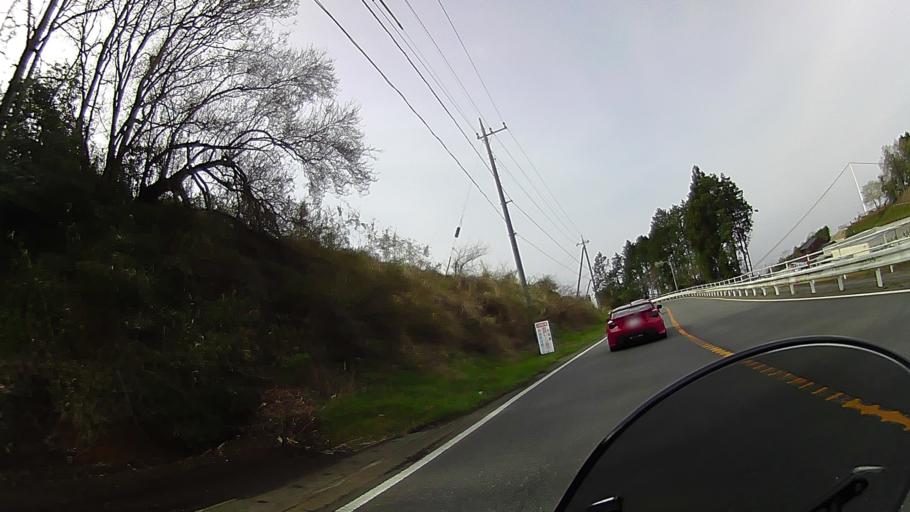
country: JP
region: Kanagawa
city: Hakone
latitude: 35.1505
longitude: 138.9843
